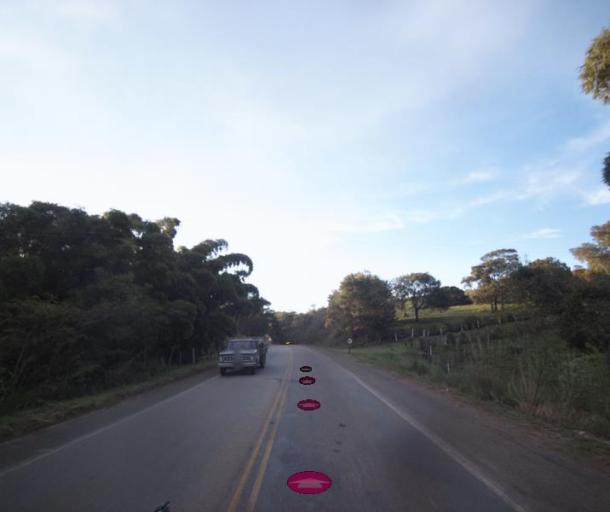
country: BR
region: Goias
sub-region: Abadiania
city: Abadiania
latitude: -16.1325
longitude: -48.8931
